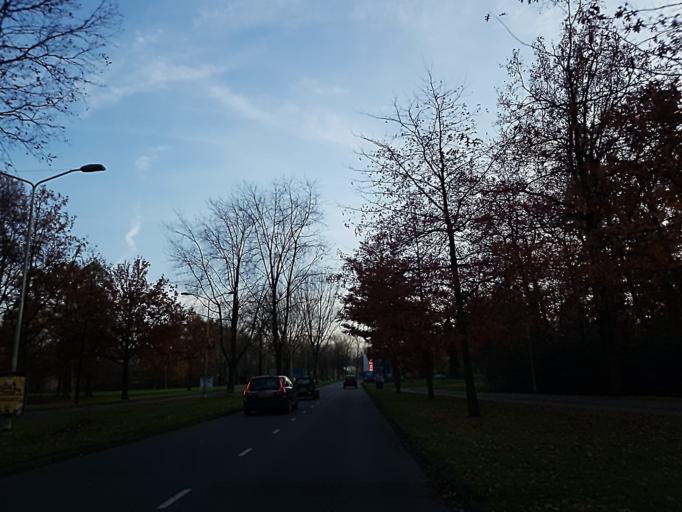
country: NL
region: North Brabant
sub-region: Roosendaal
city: Roosendaal
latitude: 51.5286
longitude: 4.4649
